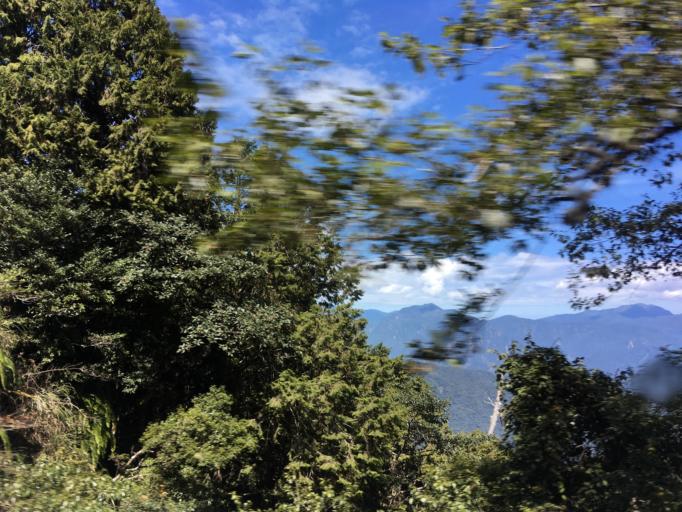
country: TW
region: Taiwan
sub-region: Yilan
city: Yilan
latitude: 24.5139
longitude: 121.5218
